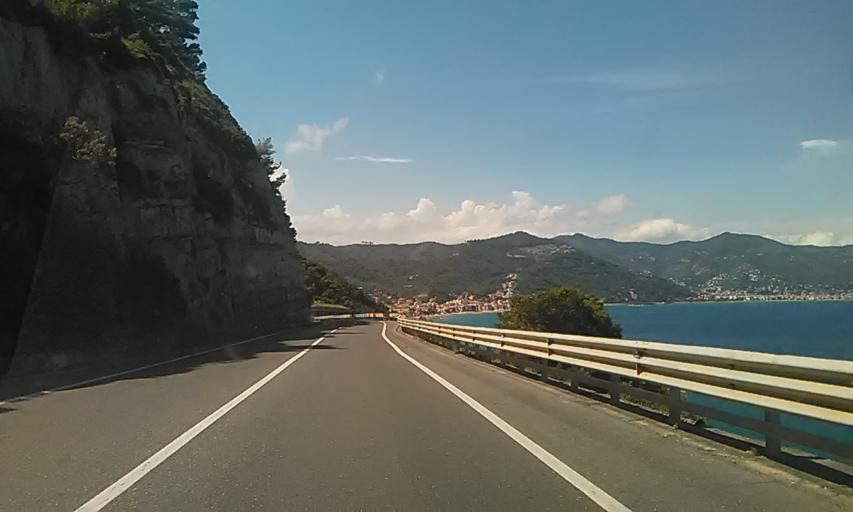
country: IT
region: Liguria
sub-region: Provincia di Savona
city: Marina di Andora
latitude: 43.9607
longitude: 8.1696
